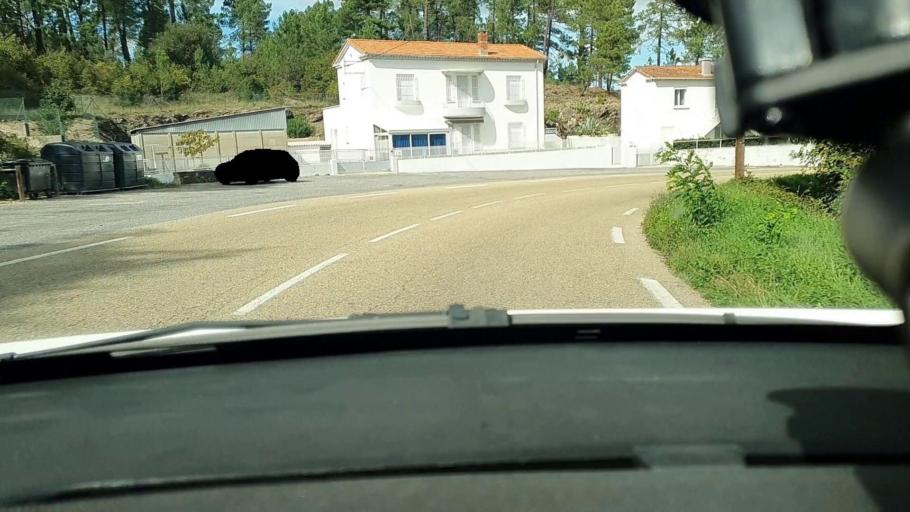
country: FR
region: Languedoc-Roussillon
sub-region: Departement du Gard
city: Laval-Pradel
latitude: 44.2386
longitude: 4.0557
